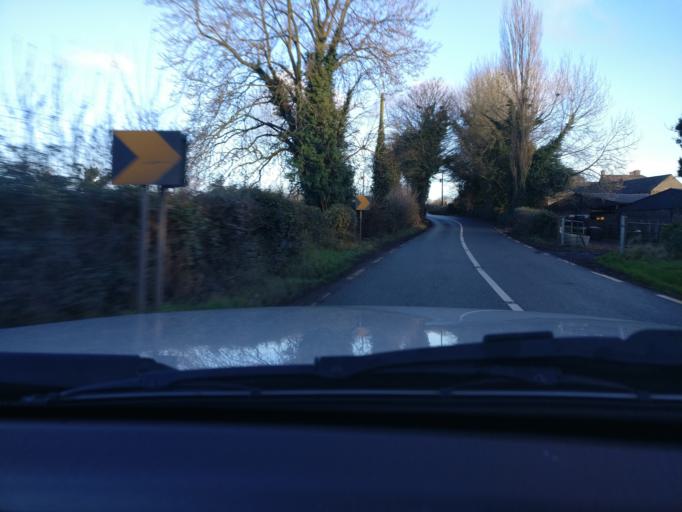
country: IE
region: Leinster
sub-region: An Mhi
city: Navan
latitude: 53.7971
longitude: -6.7076
